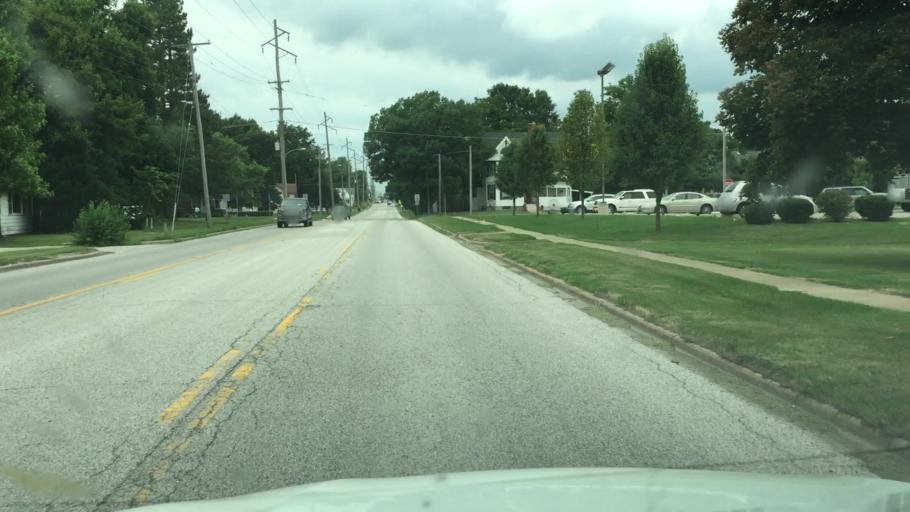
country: US
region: Illinois
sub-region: Hancock County
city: Carthage
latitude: 40.4162
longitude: -91.1263
